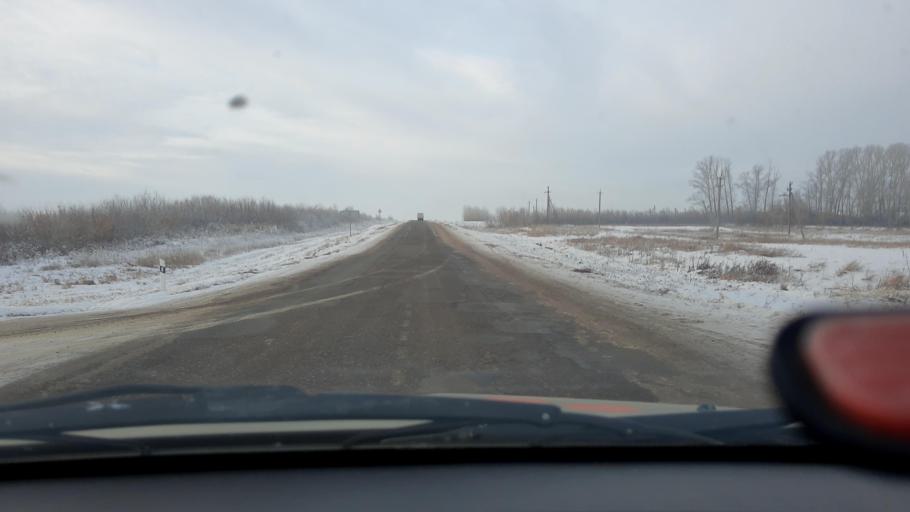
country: RU
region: Bashkortostan
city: Avdon
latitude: 54.3650
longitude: 55.8292
